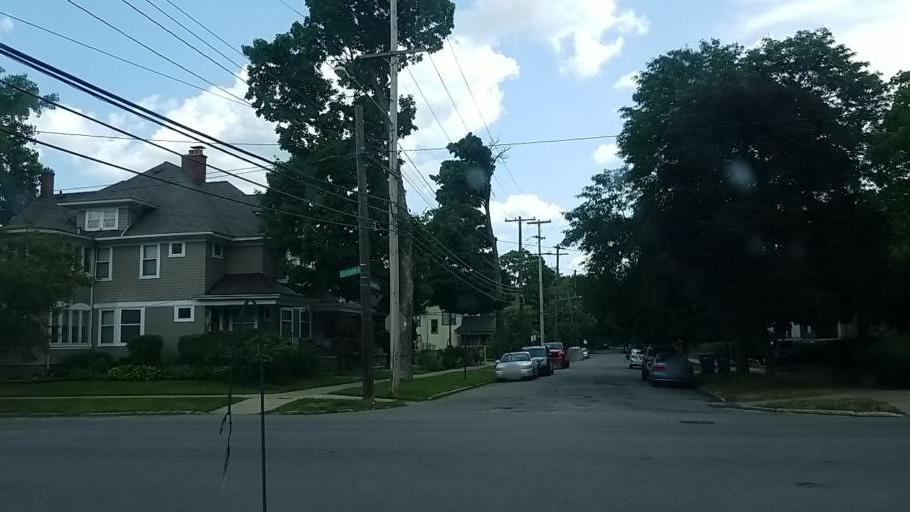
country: US
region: Michigan
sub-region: Kent County
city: Grand Rapids
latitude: 42.9689
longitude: -85.6621
